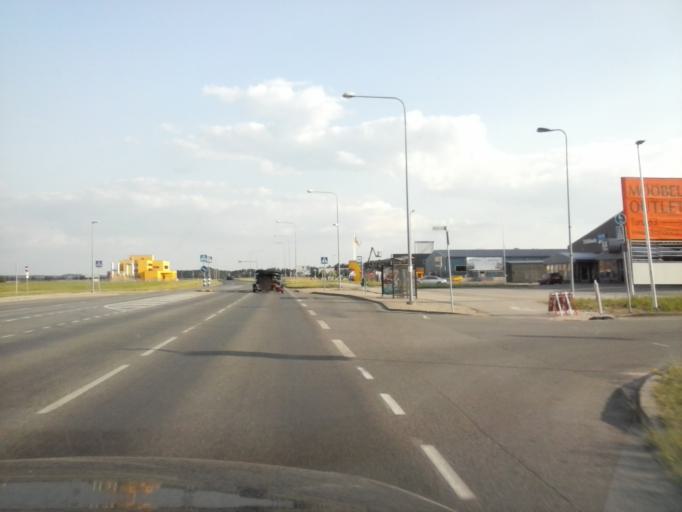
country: EE
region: Tartu
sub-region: UElenurme vald
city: Ulenurme
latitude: 58.3457
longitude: 26.7412
